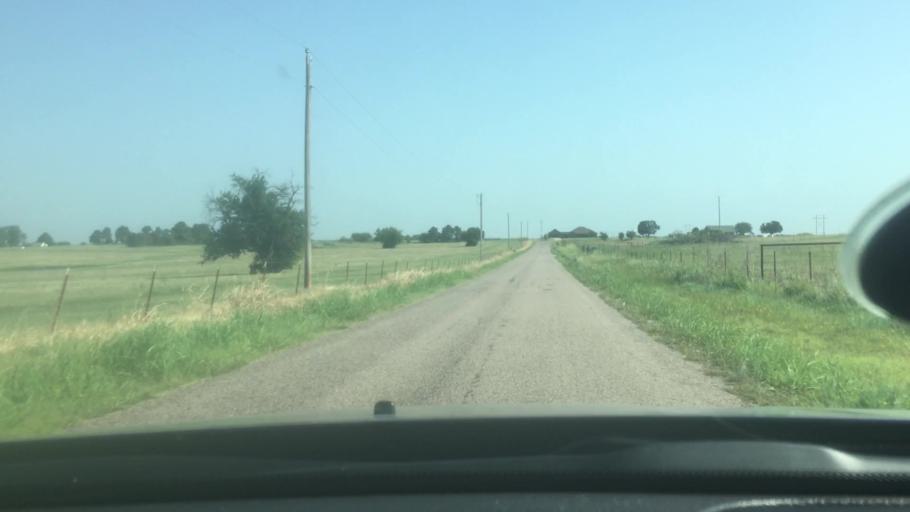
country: US
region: Oklahoma
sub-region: Bryan County
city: Calera
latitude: 33.9512
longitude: -96.4613
